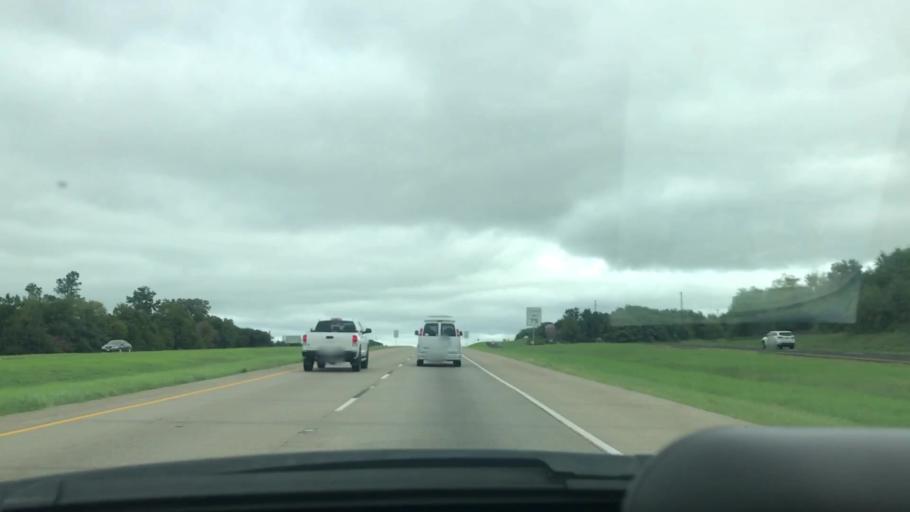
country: US
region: Texas
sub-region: Grayson County
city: Denison
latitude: 33.7381
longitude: -96.5852
